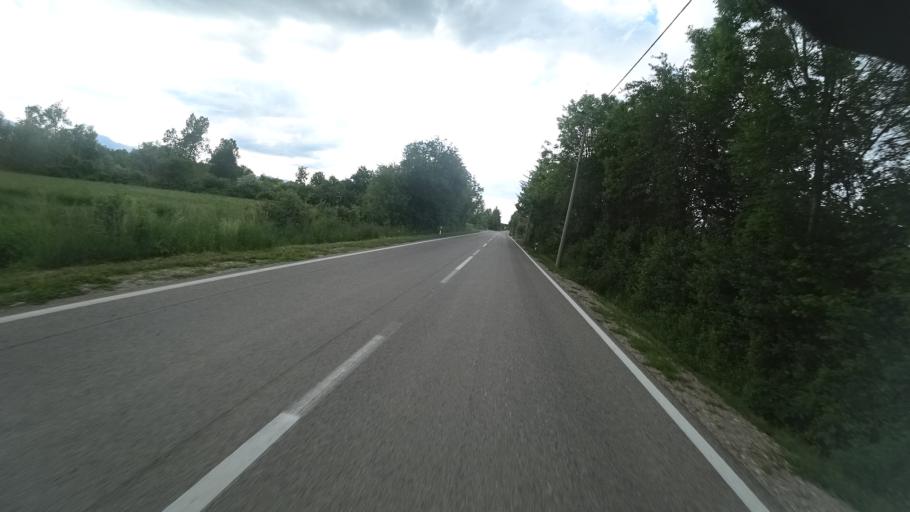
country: HR
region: Licko-Senjska
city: Gospic
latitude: 44.4867
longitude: 15.4657
